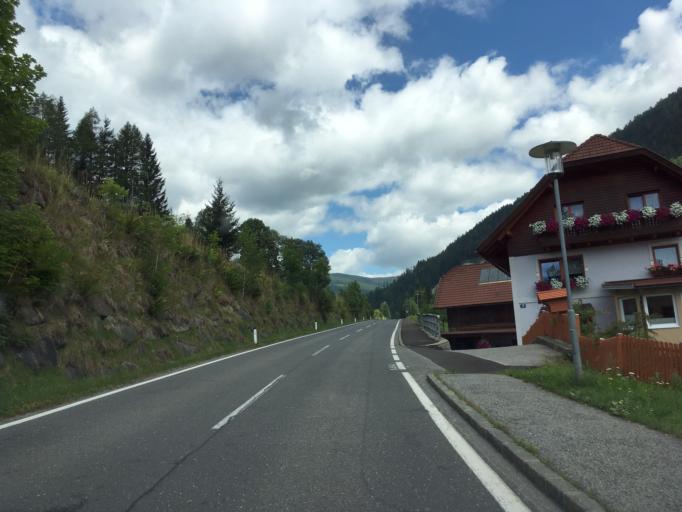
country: AT
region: Carinthia
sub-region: Politischer Bezirk Spittal an der Drau
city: Kleinkirchheim
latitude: 46.8218
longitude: 13.7708
